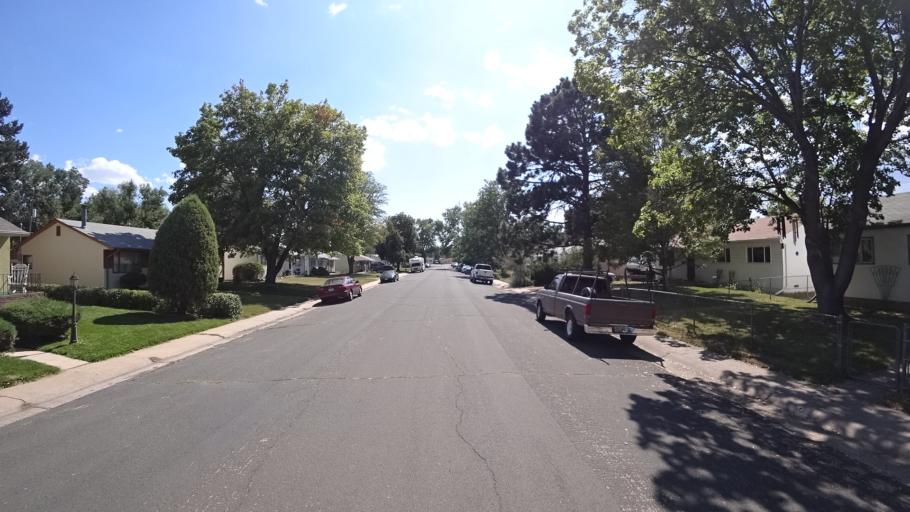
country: US
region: Colorado
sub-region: El Paso County
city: Colorado Springs
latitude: 38.8784
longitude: -104.8087
